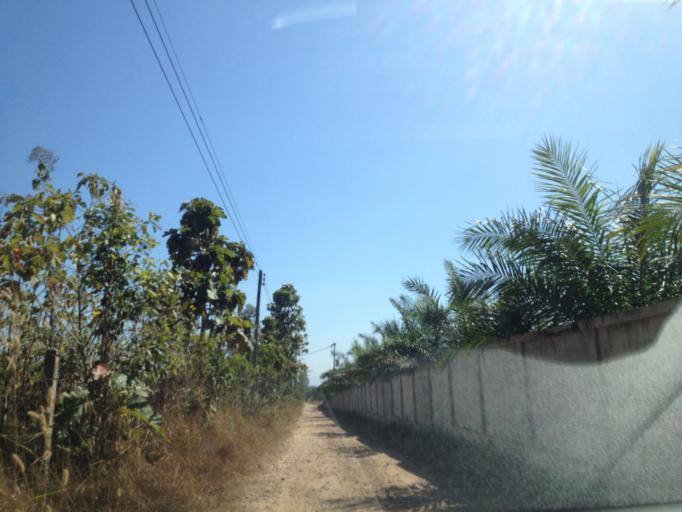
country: TH
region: Chiang Mai
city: San Pa Tong
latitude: 18.6718
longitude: 98.8693
